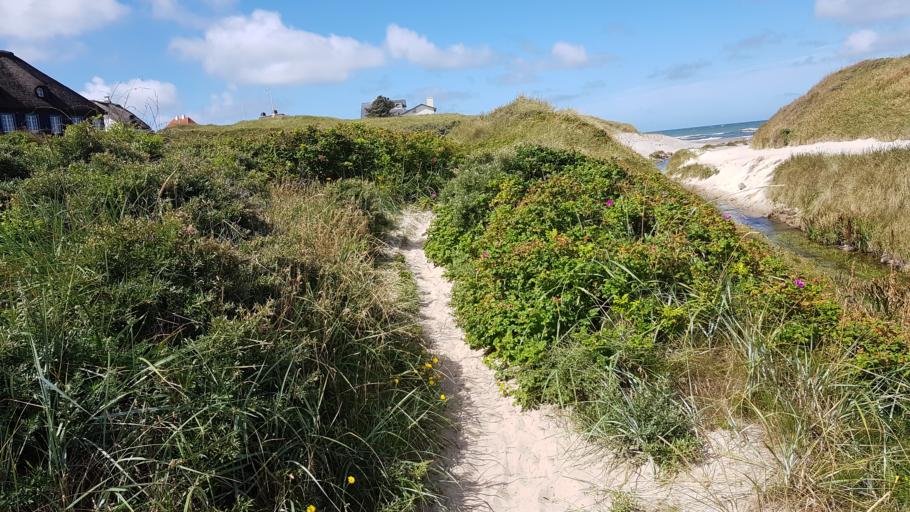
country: DK
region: North Denmark
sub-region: Jammerbugt Kommune
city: Pandrup
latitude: 57.3759
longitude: 9.7168
